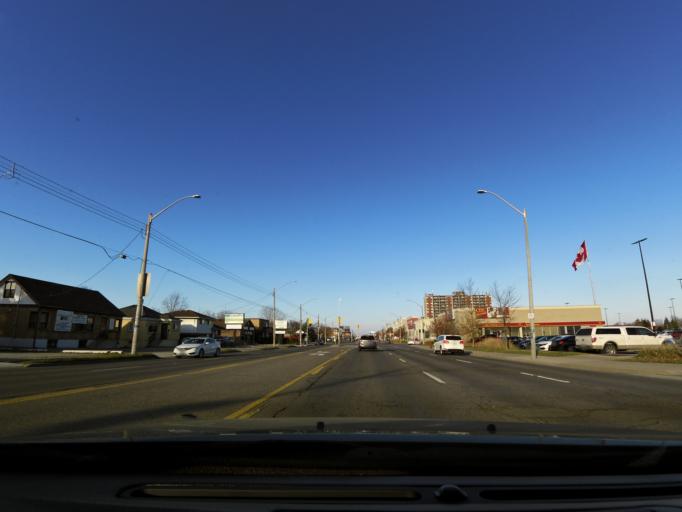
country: CA
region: Ontario
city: Hamilton
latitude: 43.2348
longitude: -79.8789
